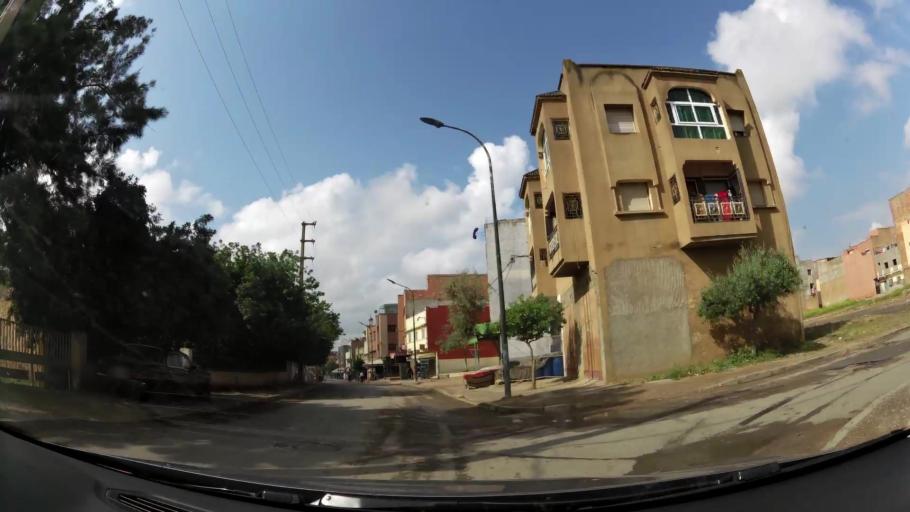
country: MA
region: Rabat-Sale-Zemmour-Zaer
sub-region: Khemisset
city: Tiflet
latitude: 33.8949
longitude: -6.3177
